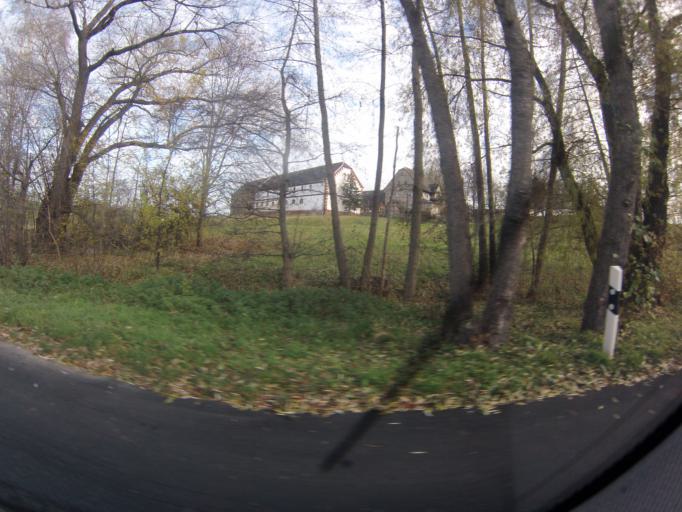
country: DE
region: Thuringia
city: Heyersdorf
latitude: 50.8528
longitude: 12.3600
